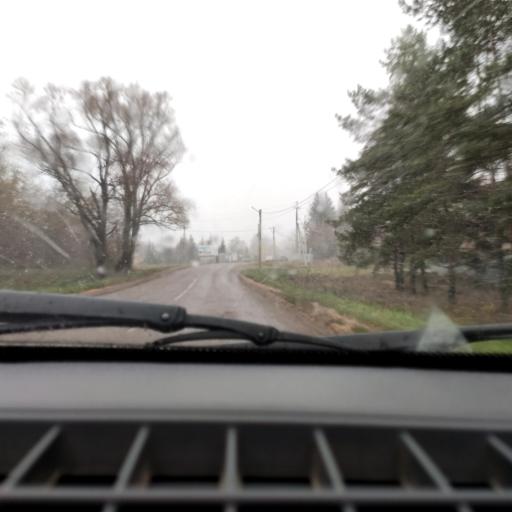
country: RU
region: Bashkortostan
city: Avdon
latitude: 54.6561
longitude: 55.7560
